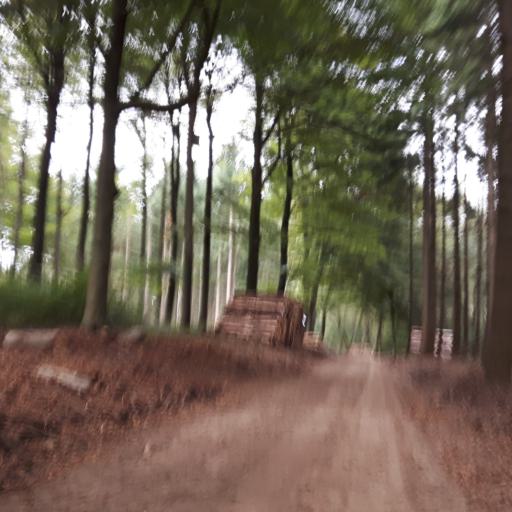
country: NL
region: Utrecht
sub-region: Gemeente Utrechtse Heuvelrug
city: Amerongen
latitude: 52.0061
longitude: 5.4916
